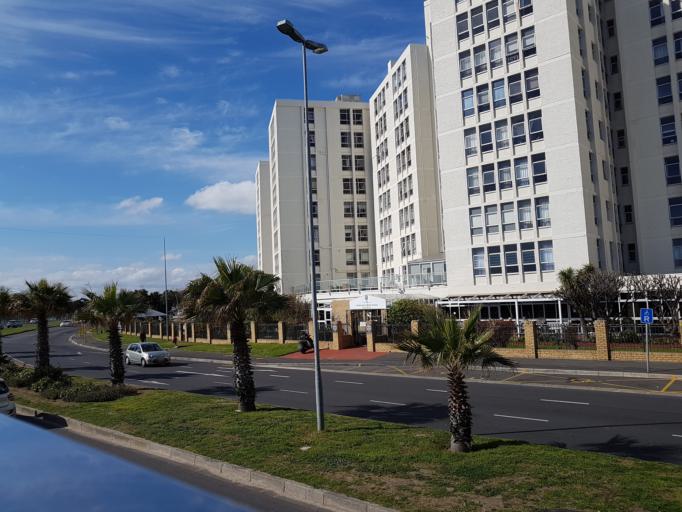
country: ZA
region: Western Cape
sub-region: City of Cape Town
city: Cape Town
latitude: -33.9066
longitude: 18.3974
